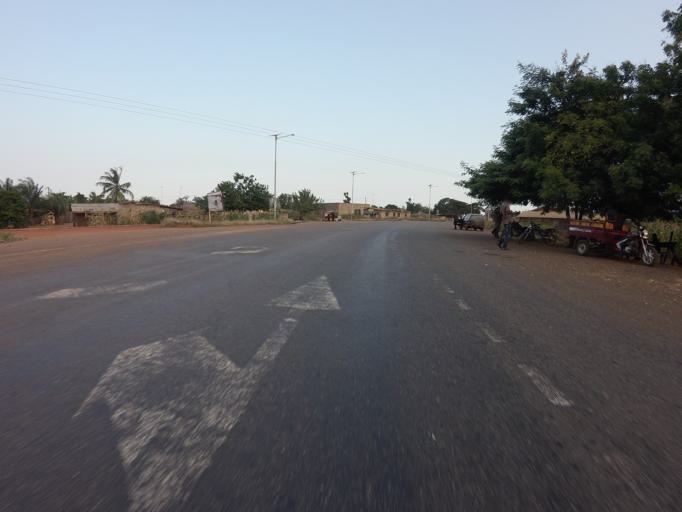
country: GH
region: Volta
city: Anloga
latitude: 6.0750
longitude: 0.6042
